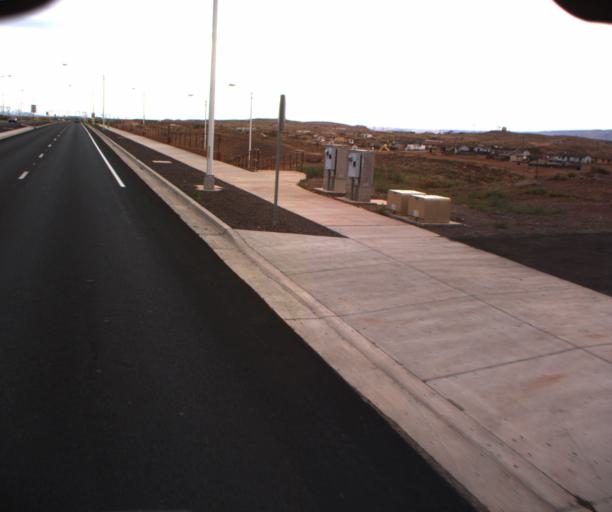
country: US
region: Arizona
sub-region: Coconino County
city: Tuba City
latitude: 35.8531
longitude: -111.4266
